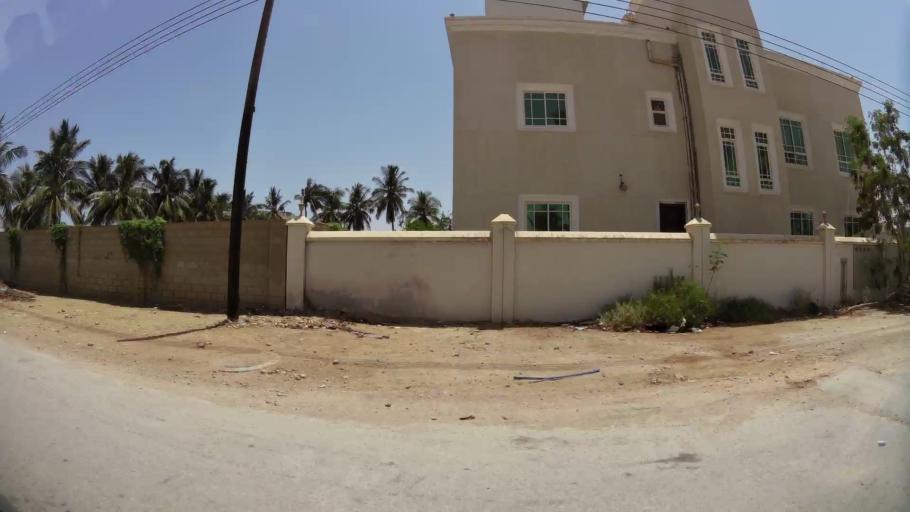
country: OM
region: Zufar
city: Salalah
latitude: 17.0573
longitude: 54.1579
